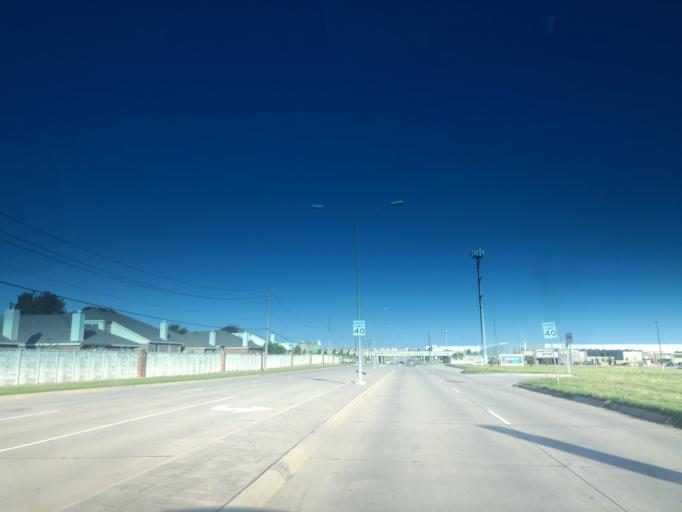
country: US
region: Texas
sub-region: Dallas County
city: Grand Prairie
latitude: 32.7055
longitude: -97.0204
